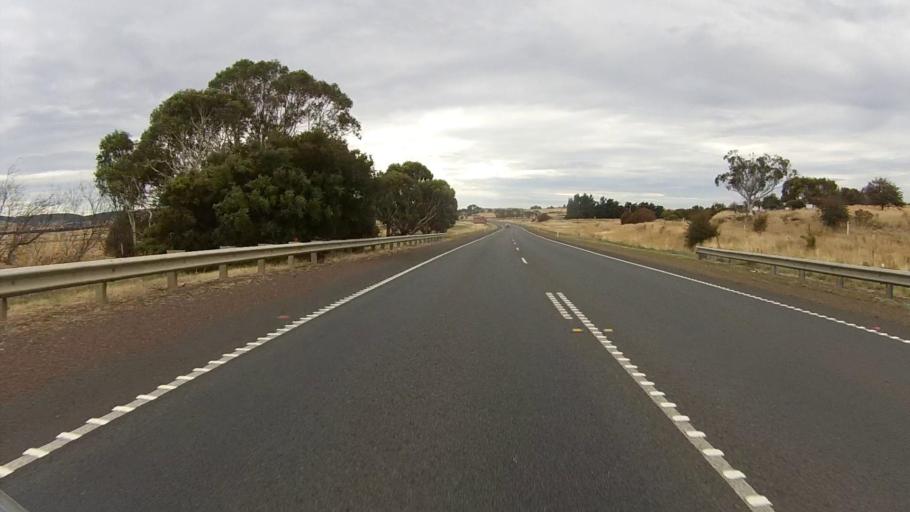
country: AU
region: Tasmania
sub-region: Brighton
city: Bridgewater
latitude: -42.3207
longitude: 147.3470
